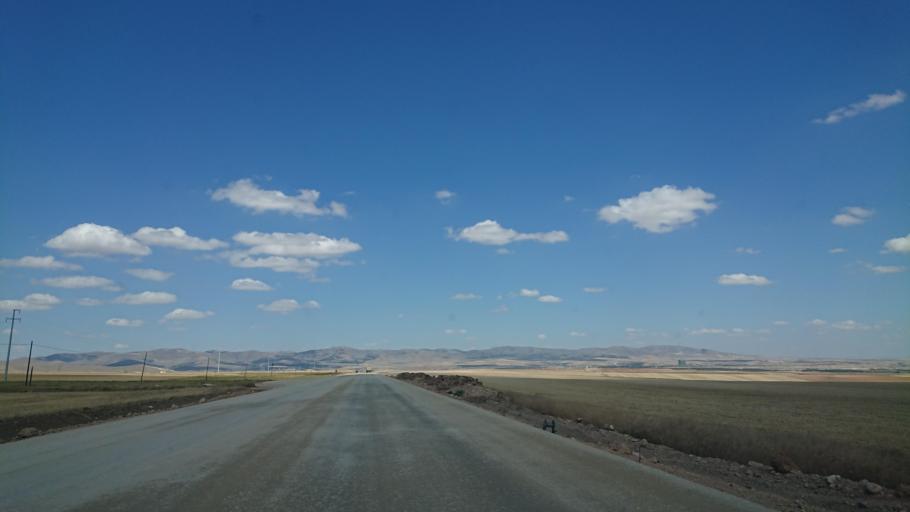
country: TR
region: Kirsehir
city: Kirsehir
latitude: 39.1383
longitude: 34.0611
